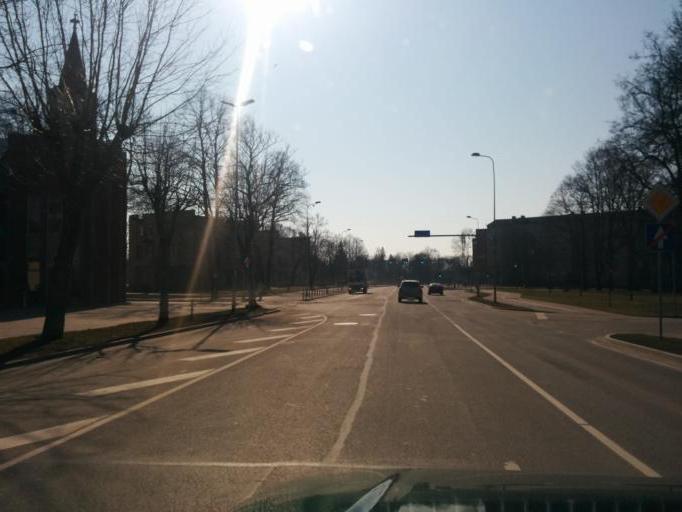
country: LV
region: Jelgava
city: Jelgava
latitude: 56.6450
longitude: 23.7273
